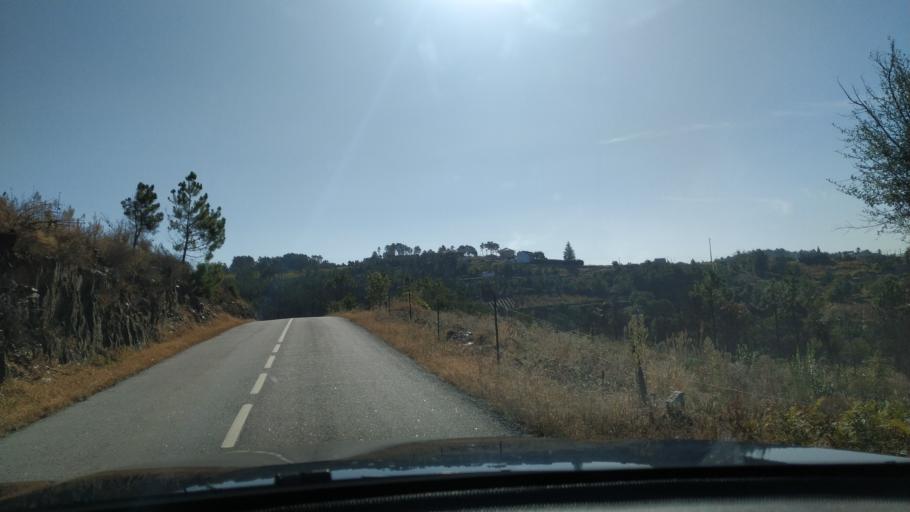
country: PT
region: Vila Real
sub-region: Sabrosa
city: Vilela
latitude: 41.2327
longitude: -7.6352
